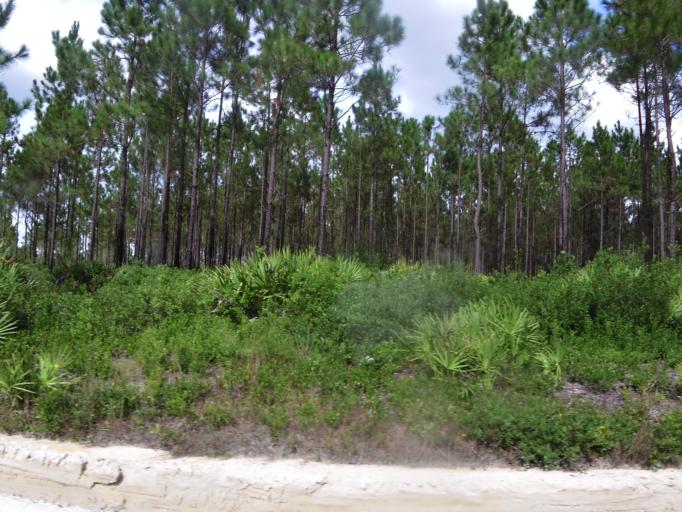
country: US
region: Florida
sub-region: Nassau County
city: Hilliard
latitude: 30.5955
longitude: -82.0582
